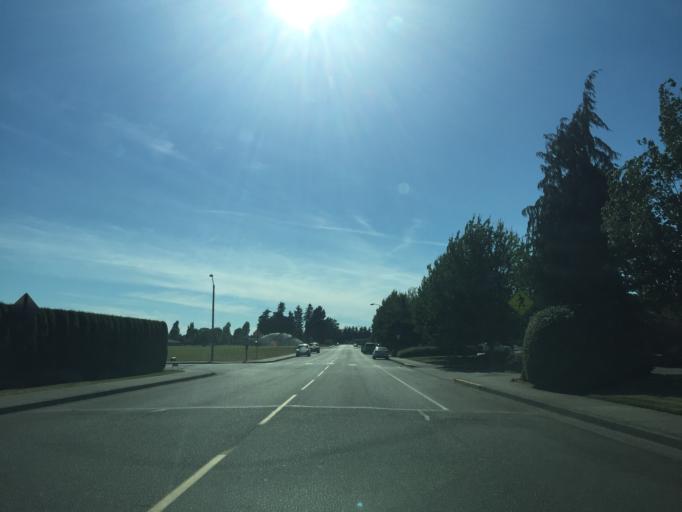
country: US
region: Washington
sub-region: Whatcom County
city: Lynden
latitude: 48.9625
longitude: -122.4348
